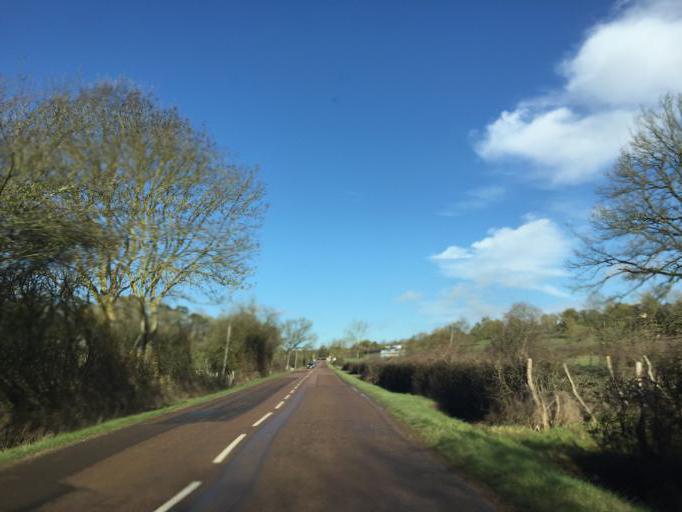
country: FR
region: Bourgogne
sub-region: Departement de la Nievre
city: Clamecy
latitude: 47.4669
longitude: 3.4505
